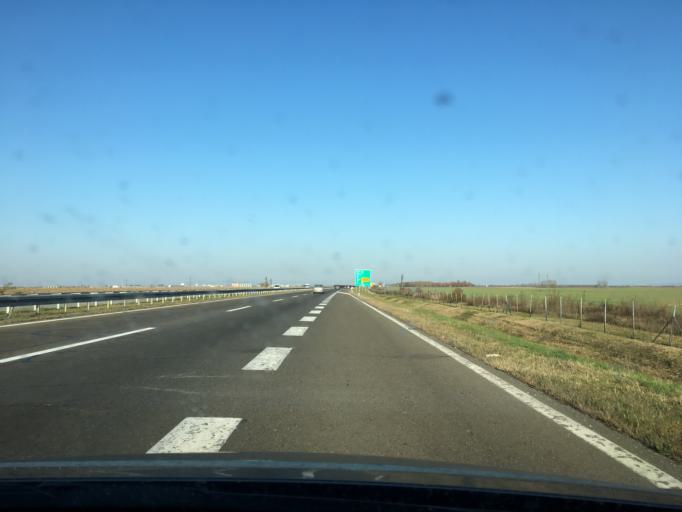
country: RS
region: Autonomna Pokrajina Vojvodina
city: Nova Pazova
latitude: 44.9729
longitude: 20.2303
